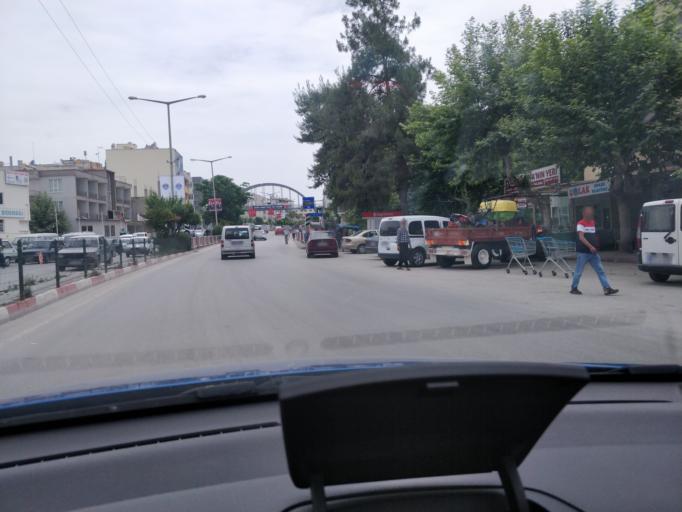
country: TR
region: Mersin
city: Mut
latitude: 36.6461
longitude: 33.4357
